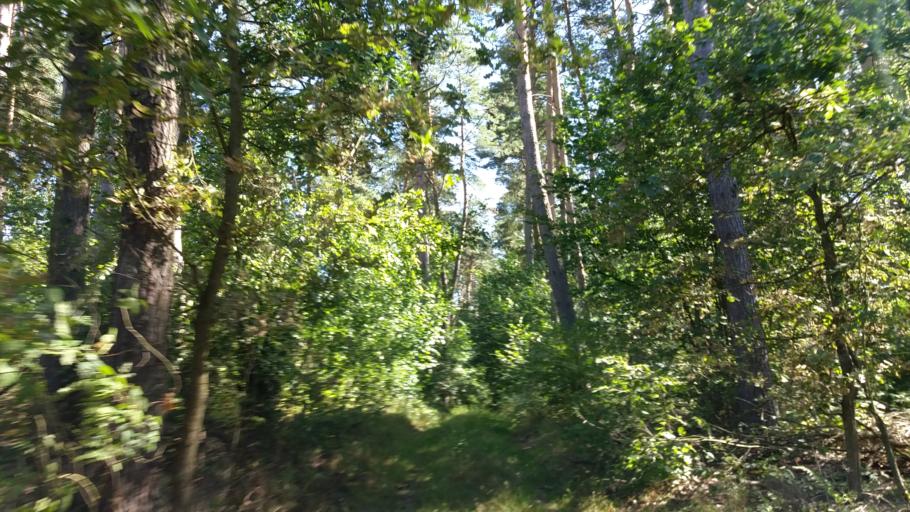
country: PL
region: West Pomeranian Voivodeship
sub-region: Powiat choszczenski
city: Krzecin
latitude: 53.0882
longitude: 15.4481
